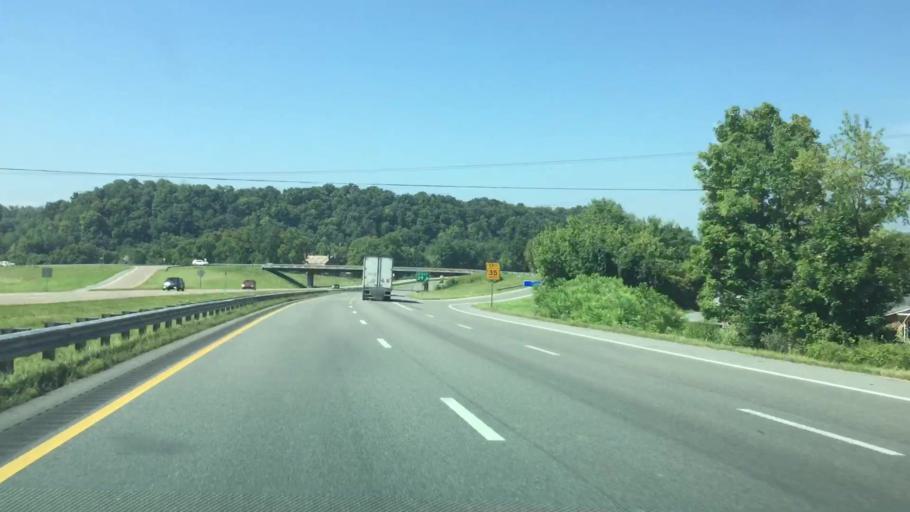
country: US
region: Virginia
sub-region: Smyth County
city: Adwolf
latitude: 36.8095
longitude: -81.6156
